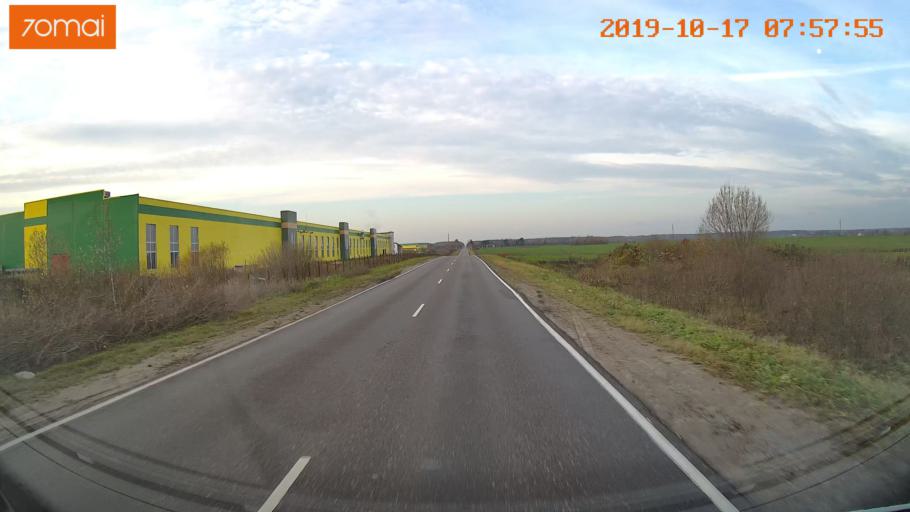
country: RU
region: Vladimir
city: Bavleny
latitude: 56.4076
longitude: 39.5677
